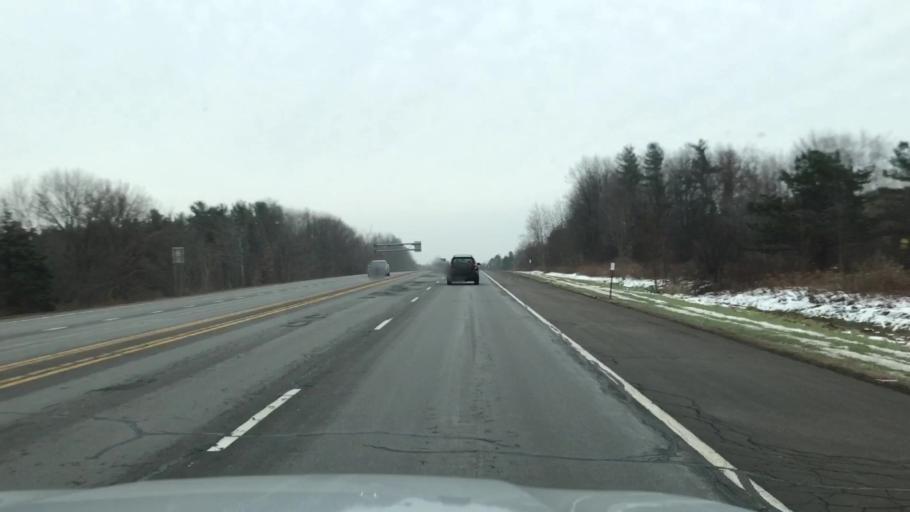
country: US
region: New York
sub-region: Erie County
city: Orchard Park
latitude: 42.7490
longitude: -78.7562
